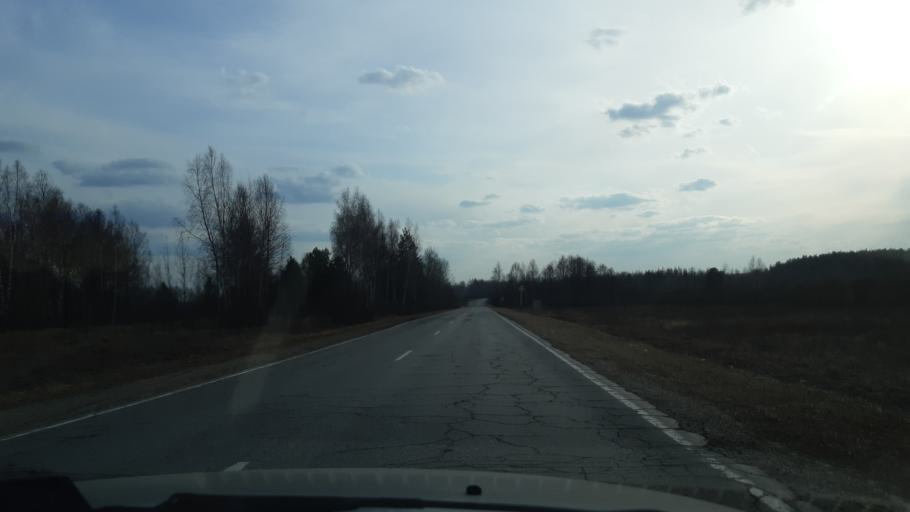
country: RU
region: Vladimir
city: Luknovo
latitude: 56.1818
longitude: 42.0127
